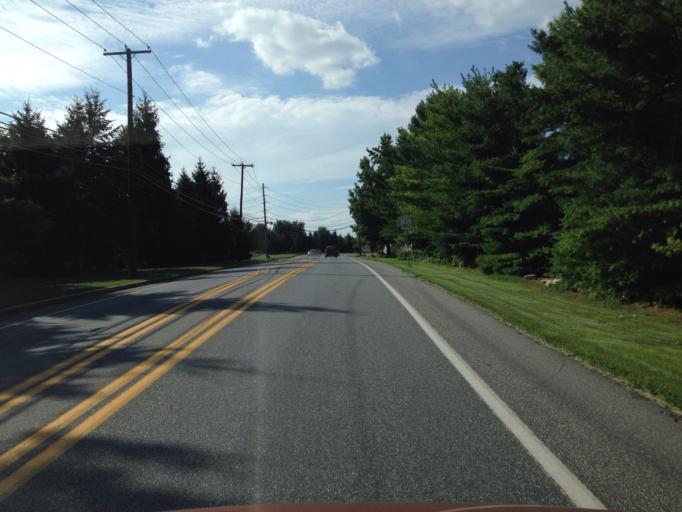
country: US
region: Pennsylvania
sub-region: Lancaster County
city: East Petersburg
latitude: 40.1156
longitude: -76.3394
